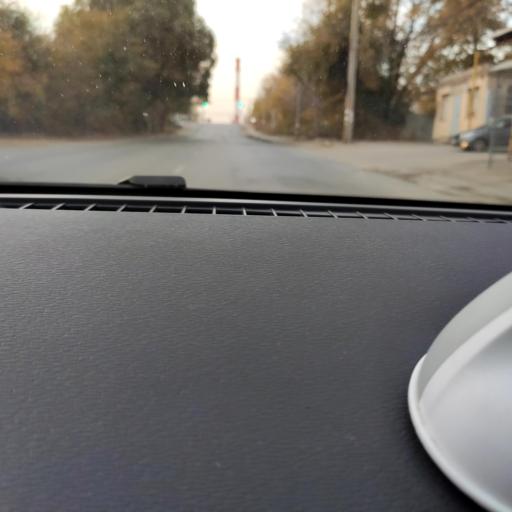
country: RU
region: Samara
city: Samara
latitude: 53.1815
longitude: 50.1650
